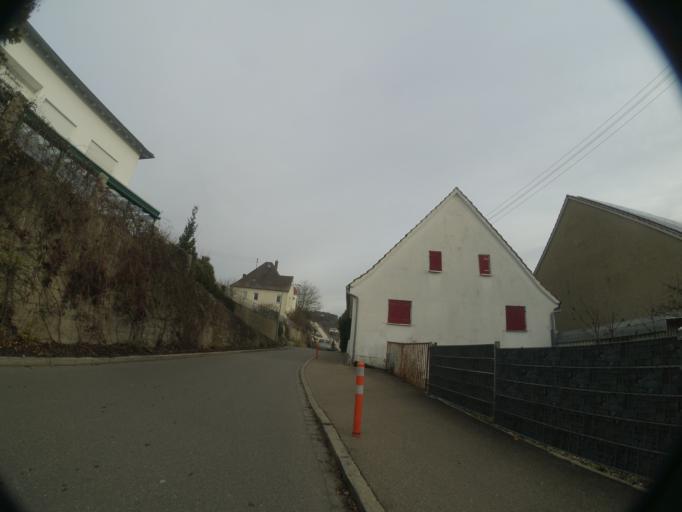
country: DE
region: Bavaria
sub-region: Swabia
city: Neu-Ulm
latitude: 48.4357
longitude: 10.0479
